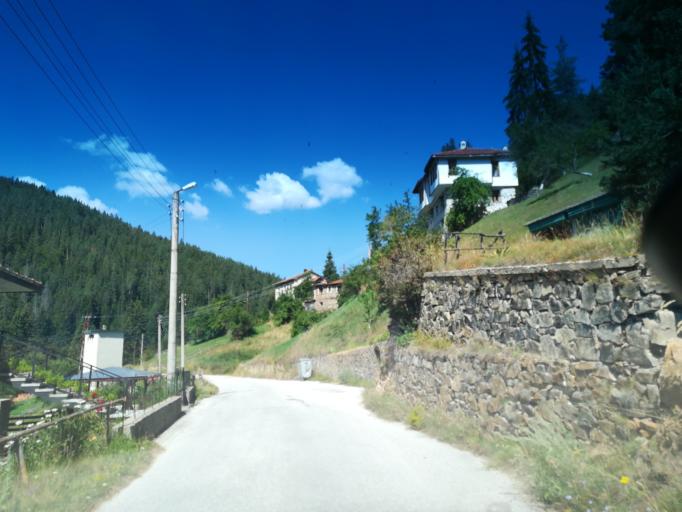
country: BG
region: Smolyan
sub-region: Obshtina Smolyan
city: Smolyan
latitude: 41.6580
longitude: 24.8216
